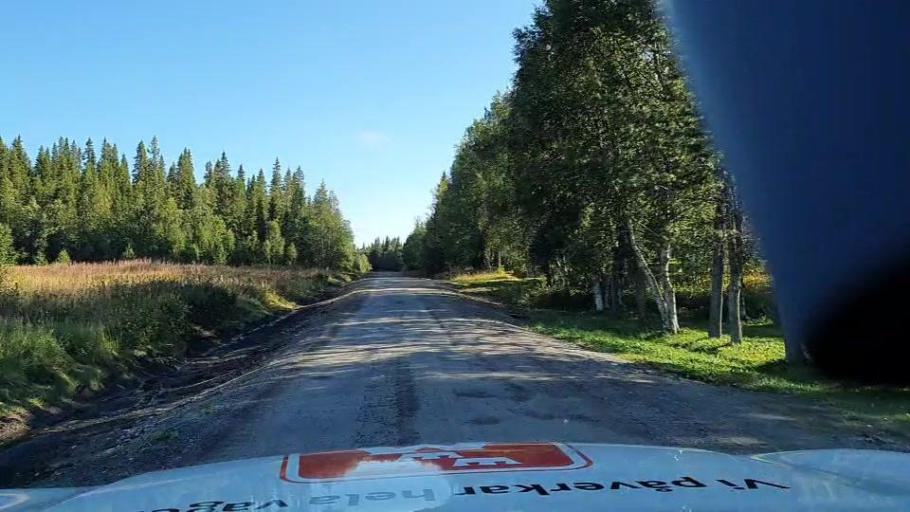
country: SE
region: Jaemtland
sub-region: Stroemsunds Kommun
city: Stroemsund
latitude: 64.5693
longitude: 15.0839
